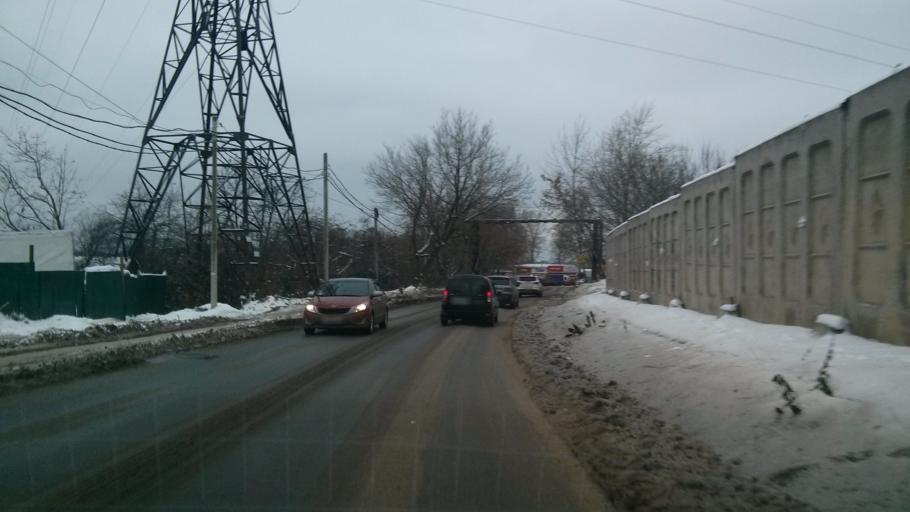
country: RU
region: Nizjnij Novgorod
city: Bor
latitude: 56.3058
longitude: 44.0625
